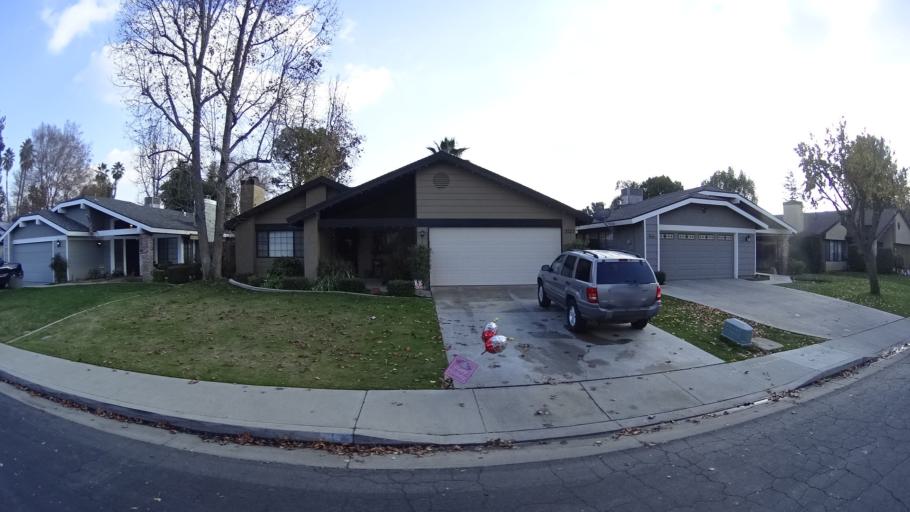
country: US
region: California
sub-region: Kern County
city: Greenacres
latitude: 35.3150
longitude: -119.1046
